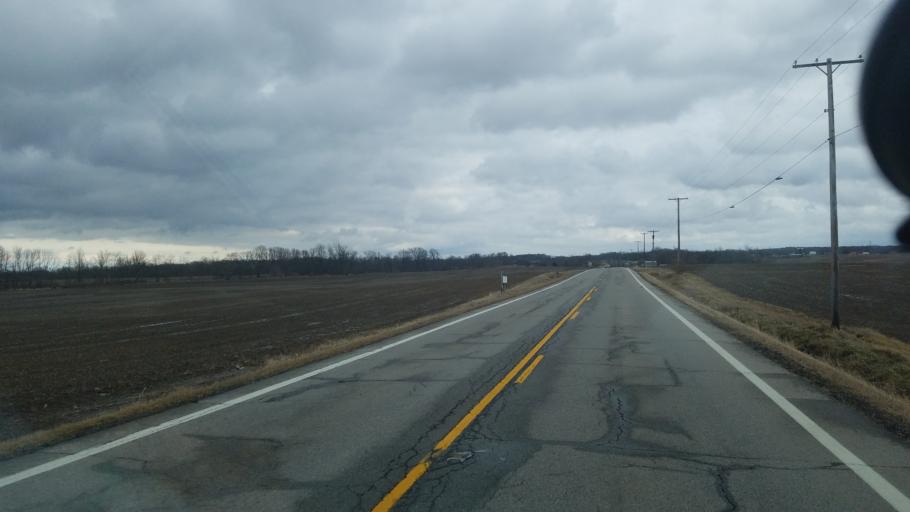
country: US
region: Ohio
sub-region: Crawford County
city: Crestline
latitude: 40.7514
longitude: -82.7208
